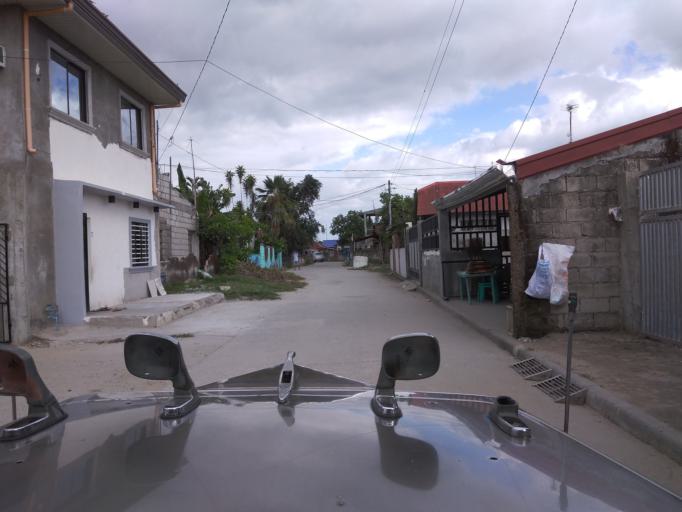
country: PH
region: Central Luzon
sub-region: Province of Pampanga
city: Pandacaqui
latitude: 15.1893
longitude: 120.6503
